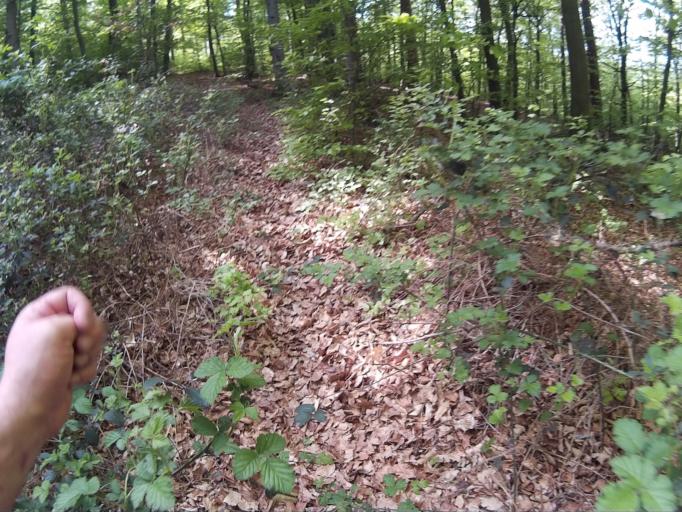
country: HU
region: Vas
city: Koszeg
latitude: 47.3593
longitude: 16.5038
